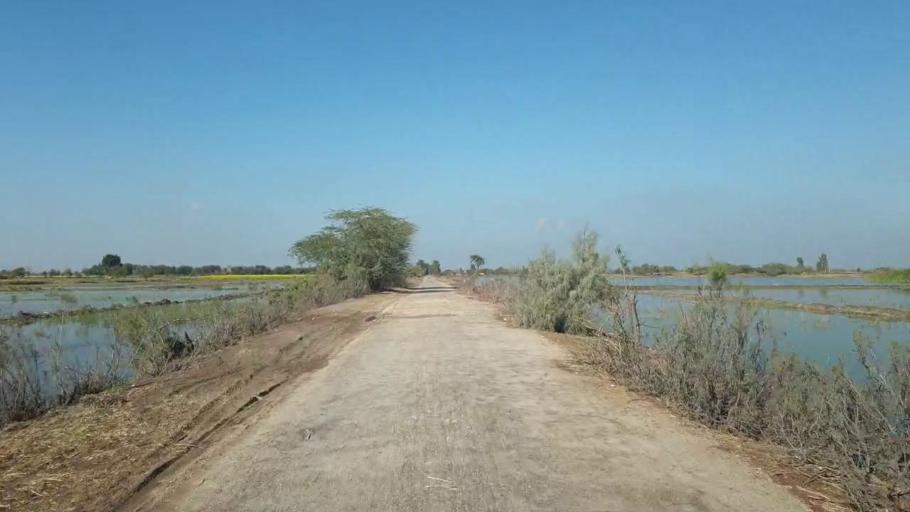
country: PK
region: Sindh
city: Shahdadpur
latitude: 25.9195
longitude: 68.5301
